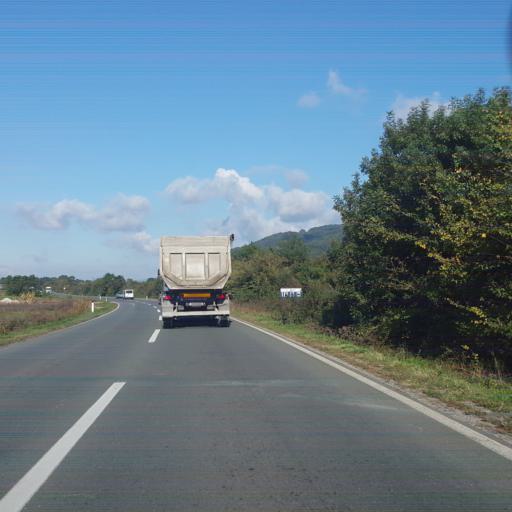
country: RS
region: Central Serbia
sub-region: Rasinski Okrug
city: Trstenik
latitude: 43.6289
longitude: 20.9711
